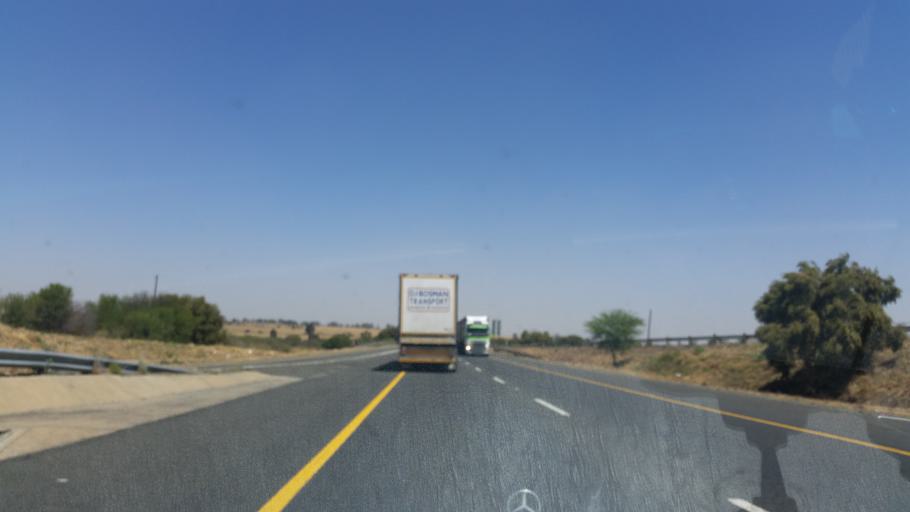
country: ZA
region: Orange Free State
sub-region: Lejweleputswa District Municipality
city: Winburg
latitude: -28.6287
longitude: 26.9080
